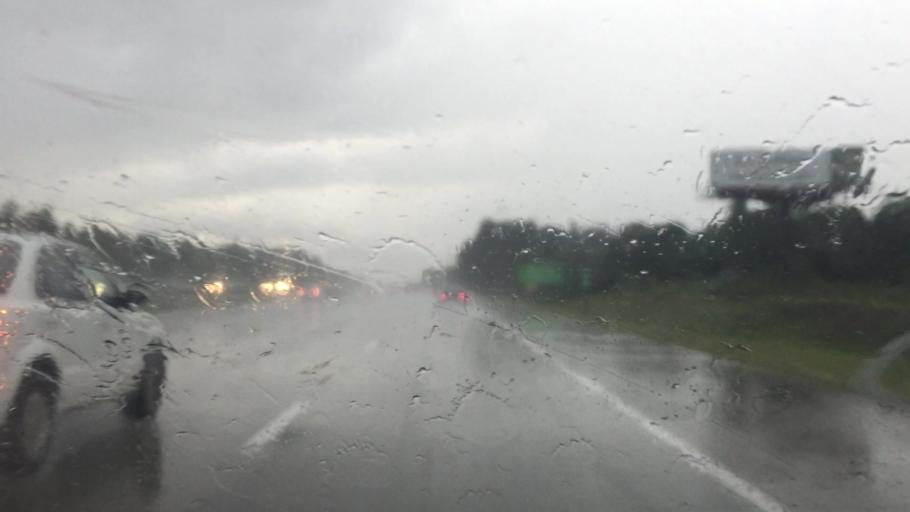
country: US
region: North Carolina
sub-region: Rowan County
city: East Spencer
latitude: 35.6715
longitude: -80.4307
